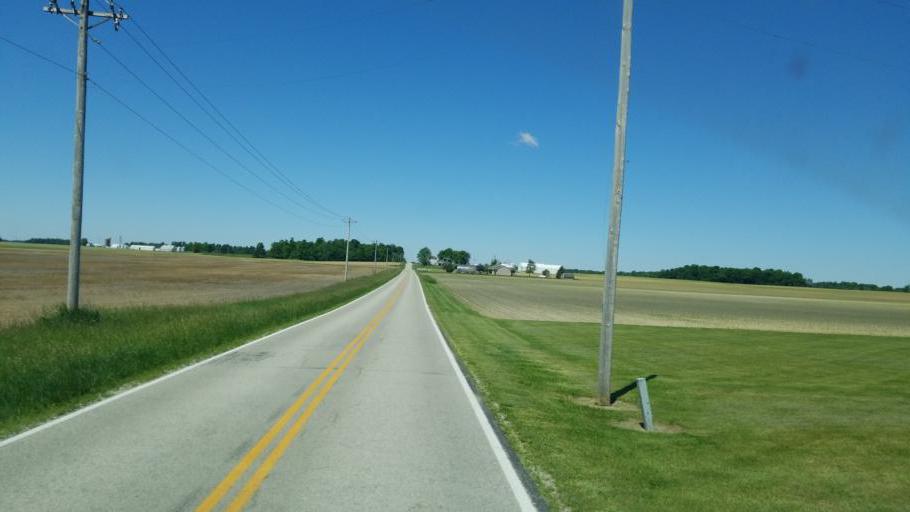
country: US
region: Ohio
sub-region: Shelby County
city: Anna
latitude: 40.3804
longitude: -84.2039
